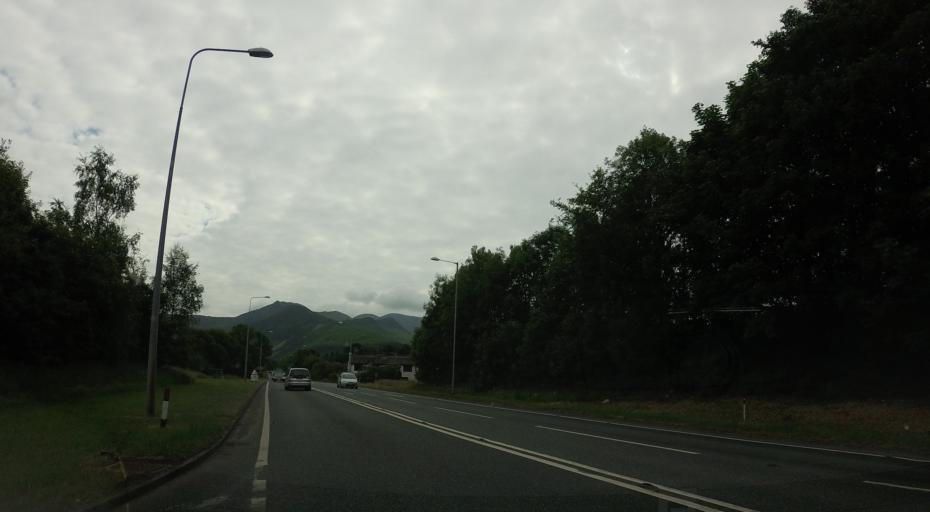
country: GB
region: England
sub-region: Cumbria
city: Keswick
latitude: 54.6055
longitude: -3.1631
